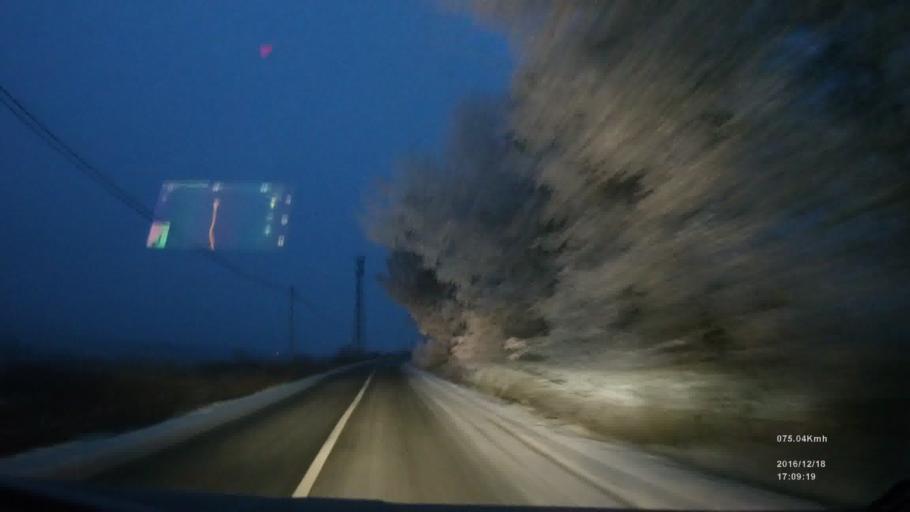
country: SK
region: Presovsky
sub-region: Okres Presov
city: Presov
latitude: 48.8749
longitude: 21.3110
